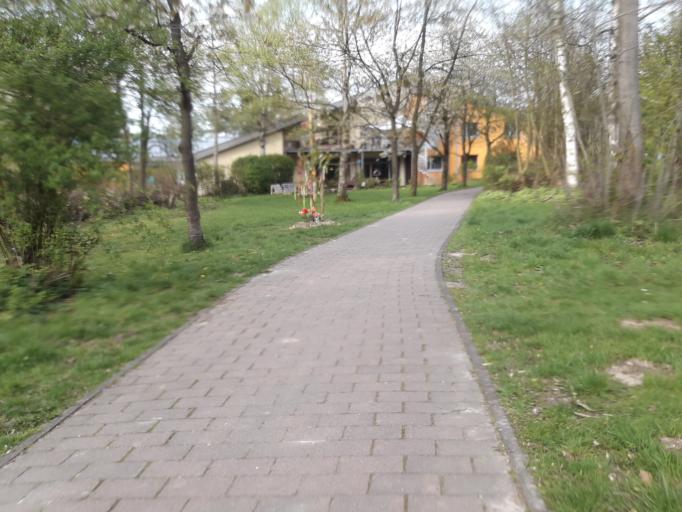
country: DE
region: North Rhine-Westphalia
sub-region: Regierungsbezirk Detmold
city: Paderborn
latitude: 51.6613
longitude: 8.7765
